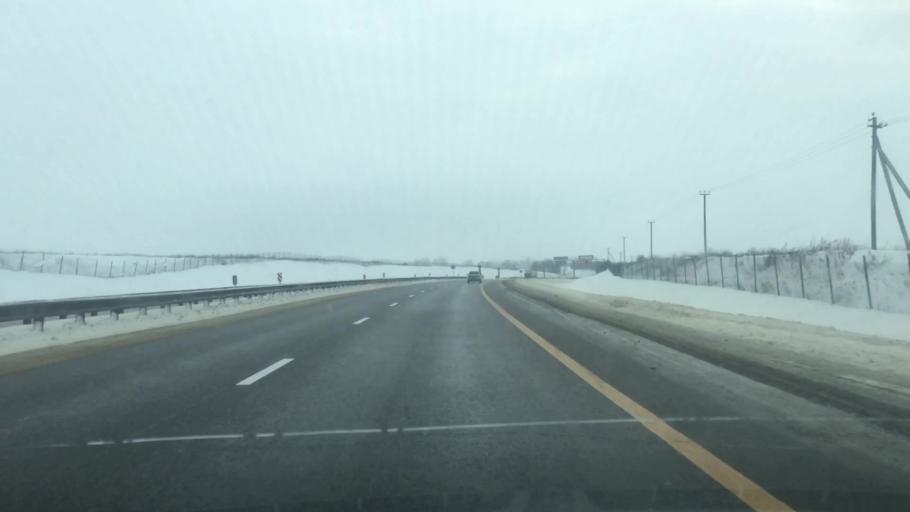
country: RU
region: Tula
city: Yefremov
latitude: 53.1398
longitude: 38.2457
